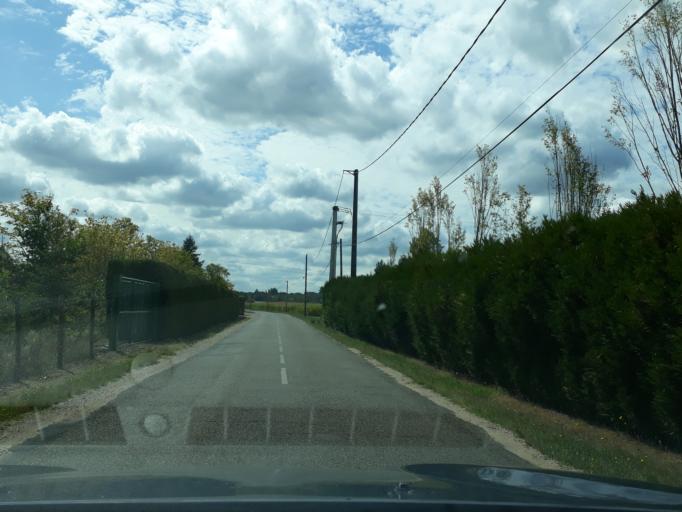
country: FR
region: Centre
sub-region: Departement du Loiret
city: Saint-Cyr-en-Val
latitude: 47.8437
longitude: 1.9721
